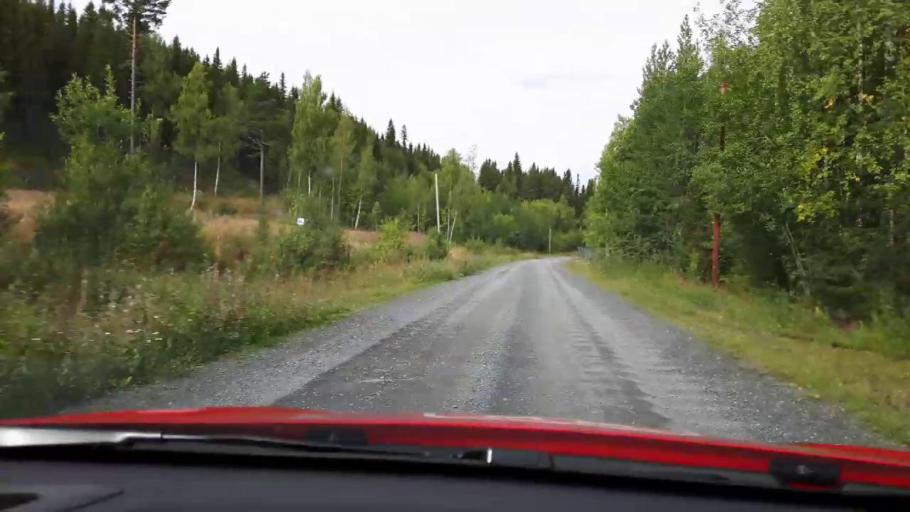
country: SE
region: Jaemtland
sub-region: Are Kommun
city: Jarpen
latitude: 63.2759
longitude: 13.7375
